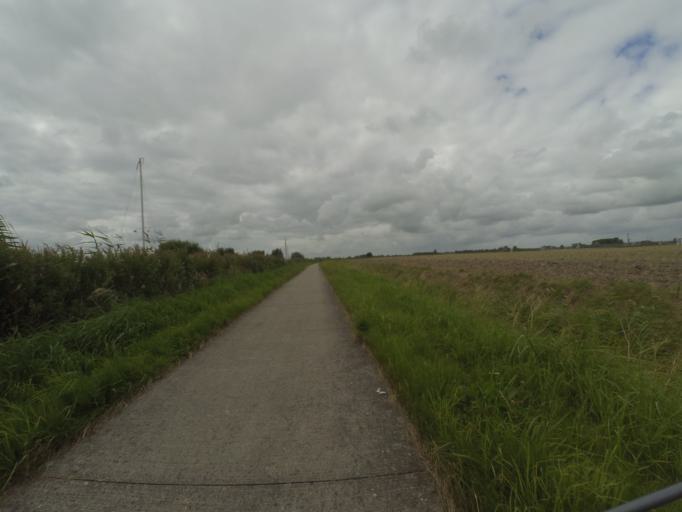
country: NL
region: Friesland
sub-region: Gemeente Kollumerland en Nieuwkruisland
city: Kollum
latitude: 53.3175
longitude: 6.1294
